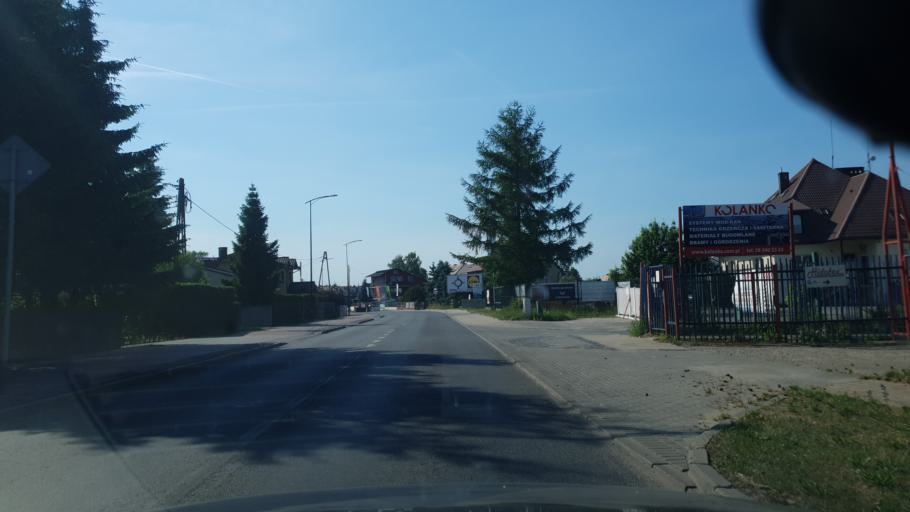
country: PL
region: Pomeranian Voivodeship
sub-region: Powiat kartuski
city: Chwaszczyno
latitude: 54.4428
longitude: 18.4235
